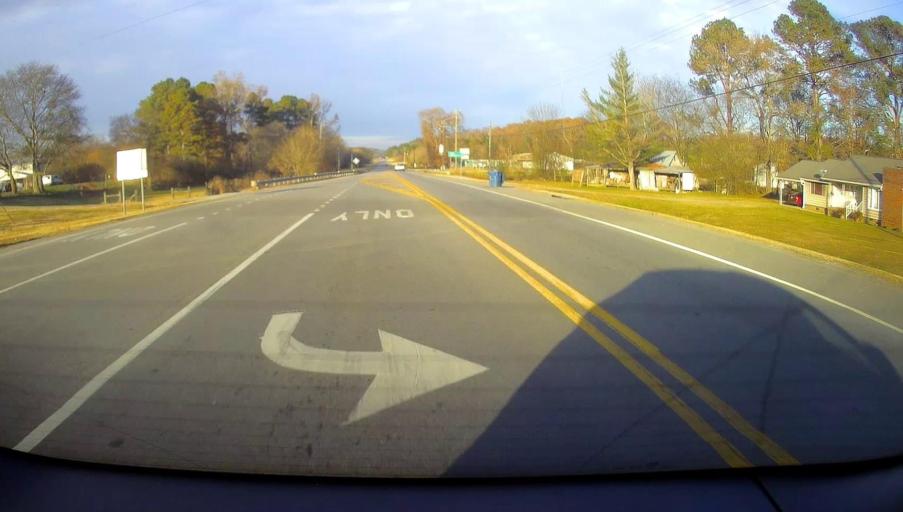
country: US
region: Alabama
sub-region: Blount County
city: Blountsville
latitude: 34.1674
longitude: -86.5161
